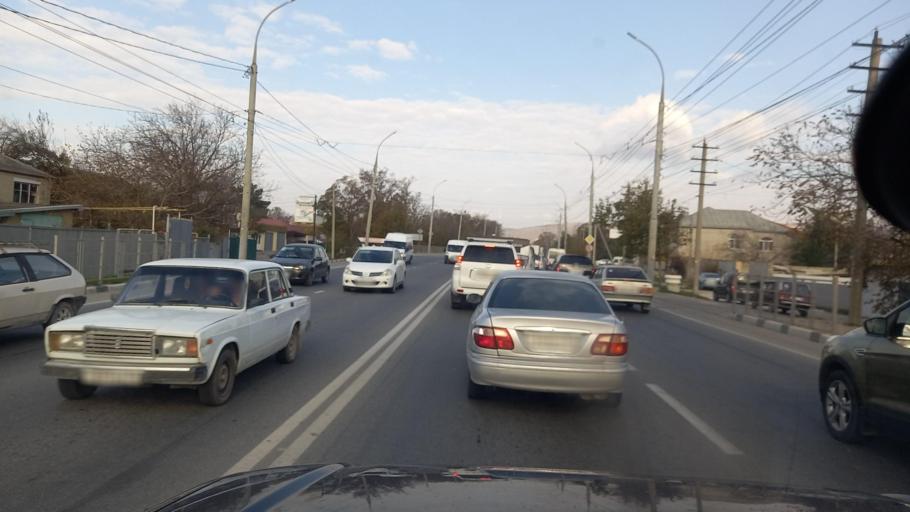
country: RU
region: Krasnodarskiy
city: Gayduk
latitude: 44.7569
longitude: 37.7250
